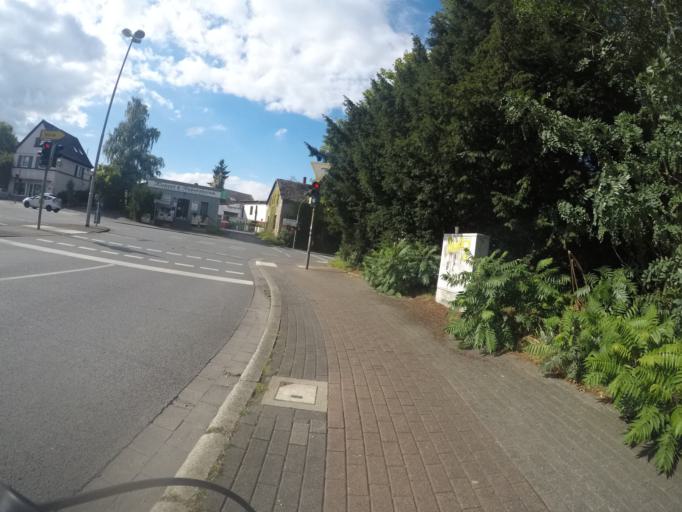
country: DE
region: North Rhine-Westphalia
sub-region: Regierungsbezirk Detmold
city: Herford
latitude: 52.1247
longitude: 8.6655
